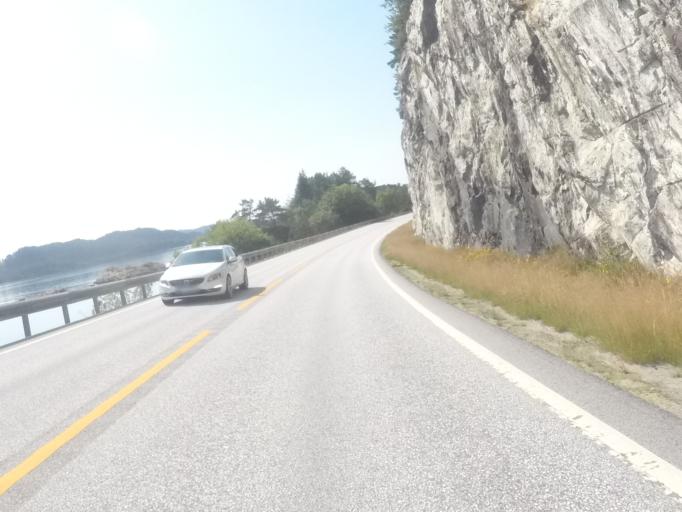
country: NO
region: Sogn og Fjordane
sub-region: Bremanger
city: Svelgen
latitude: 61.6103
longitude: 5.2254
